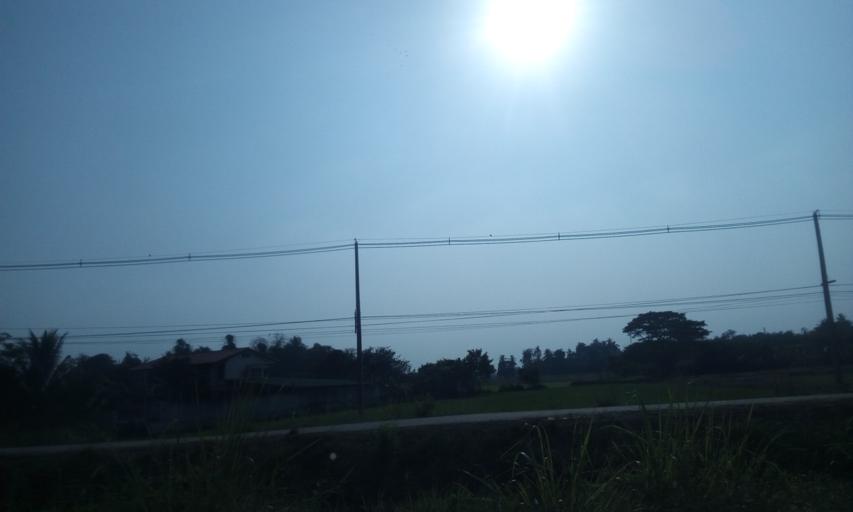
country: TH
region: Sing Buri
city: Sing Buri
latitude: 14.8585
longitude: 100.4087
